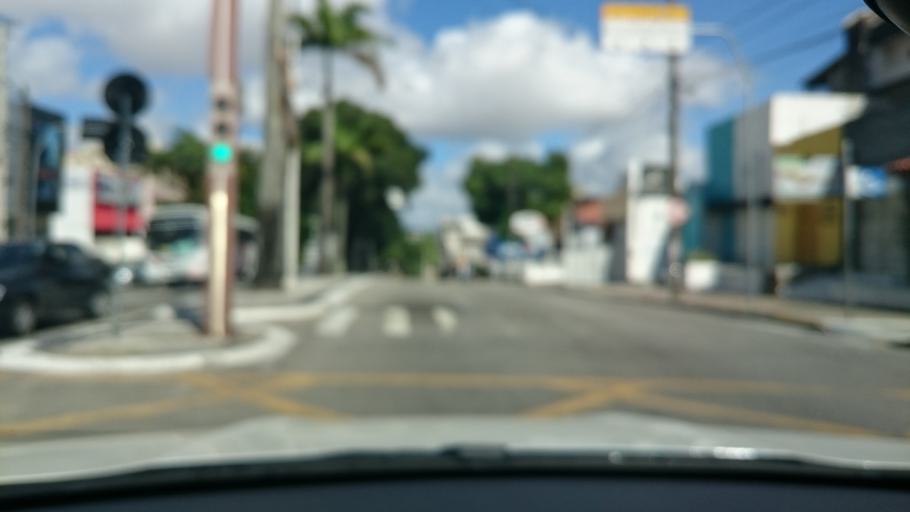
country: BR
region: Paraiba
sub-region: Campina Grande
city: Campina Grande
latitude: -7.2205
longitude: -35.8862
